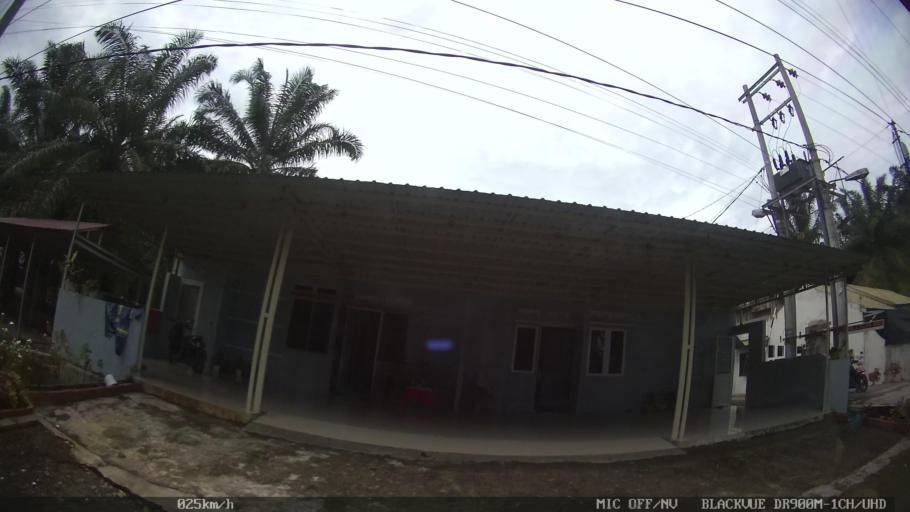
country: ID
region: North Sumatra
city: Sunggal
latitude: 3.5725
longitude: 98.5670
